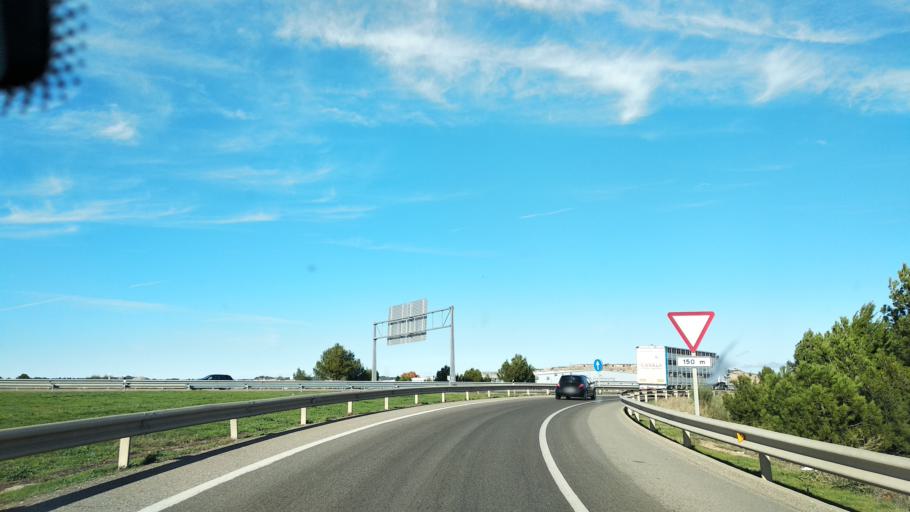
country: ES
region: Catalonia
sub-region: Provincia de Lleida
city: Alpicat
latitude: 41.6476
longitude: 0.5678
